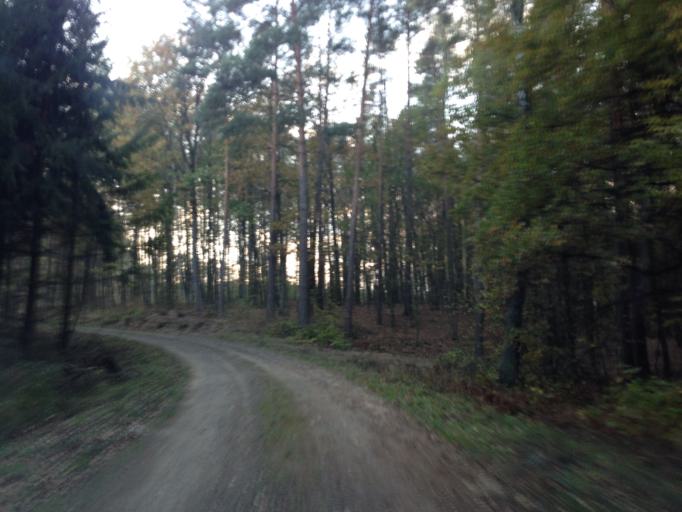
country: PL
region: Warmian-Masurian Voivodeship
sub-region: Powiat dzialdowski
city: Lidzbark
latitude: 53.2695
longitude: 19.7216
